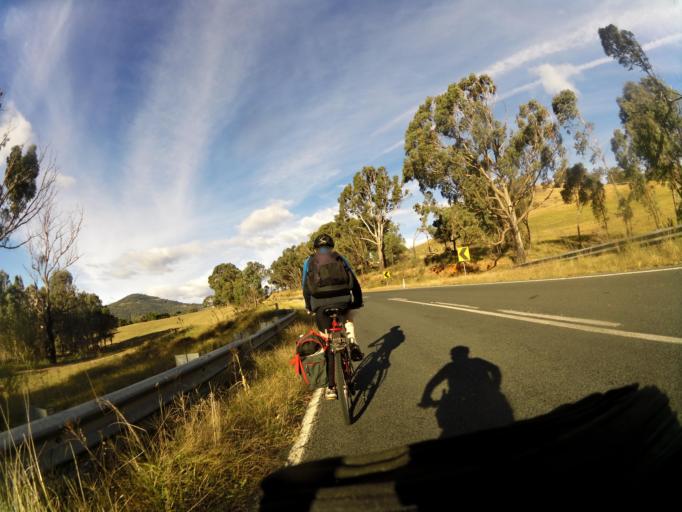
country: AU
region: New South Wales
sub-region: Greater Hume Shire
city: Holbrook
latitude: -36.0021
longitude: 147.8719
